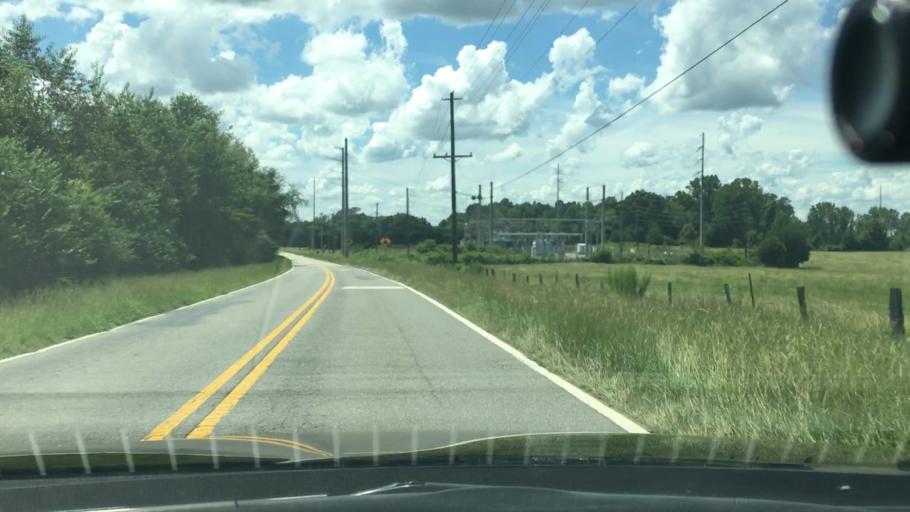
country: US
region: Georgia
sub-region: Putnam County
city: Jefferson
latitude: 33.3658
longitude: -83.2752
